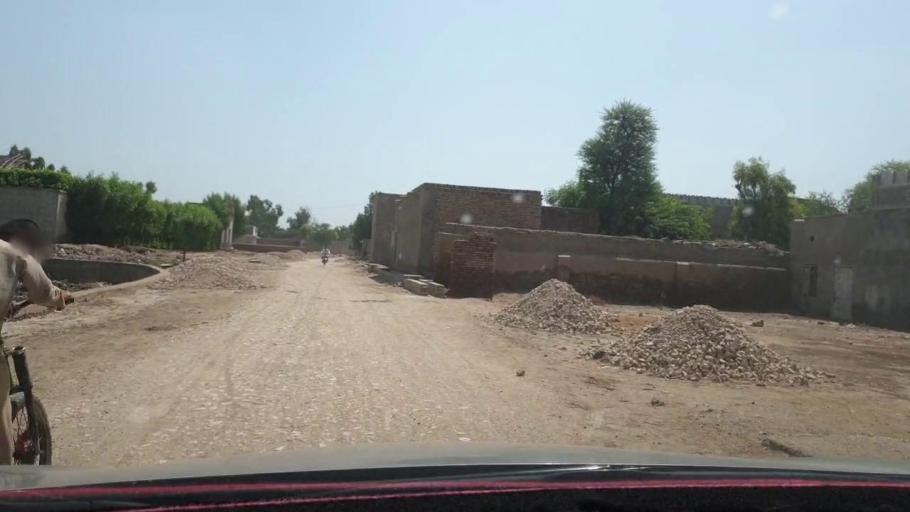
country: PK
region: Sindh
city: Warah
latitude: 27.4843
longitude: 67.8265
